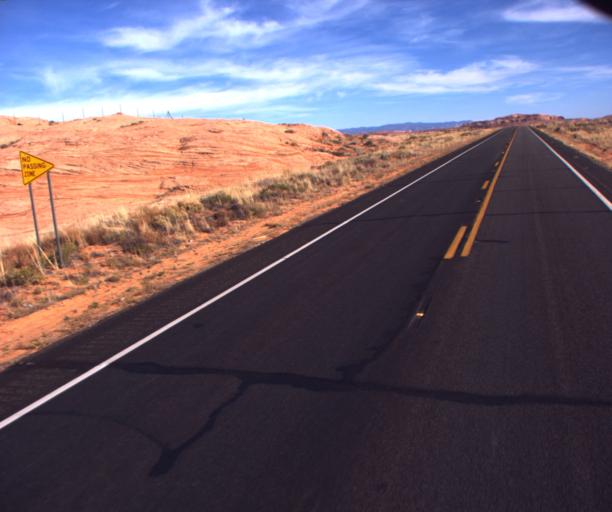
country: US
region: Arizona
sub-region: Apache County
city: Many Farms
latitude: 36.9345
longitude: -109.6315
